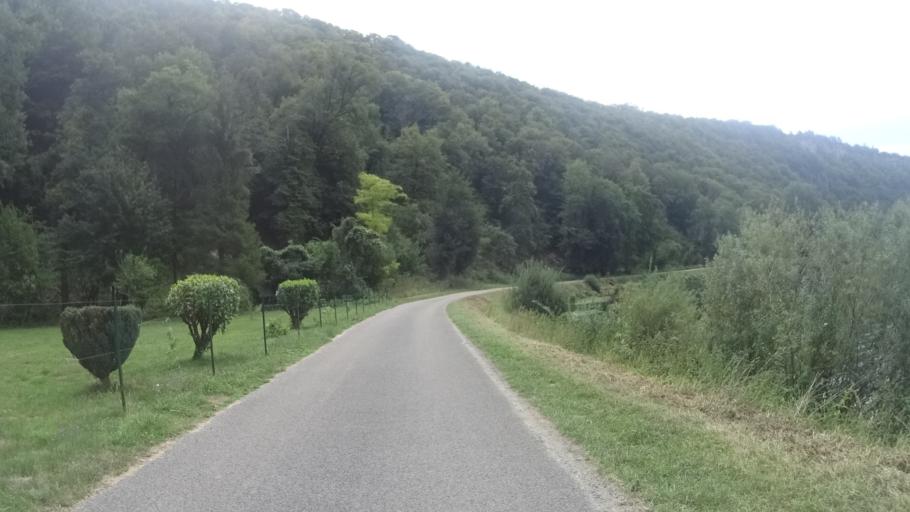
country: FR
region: Franche-Comte
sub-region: Departement du Doubs
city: Baume-les-Dames
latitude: 47.3592
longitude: 6.4192
